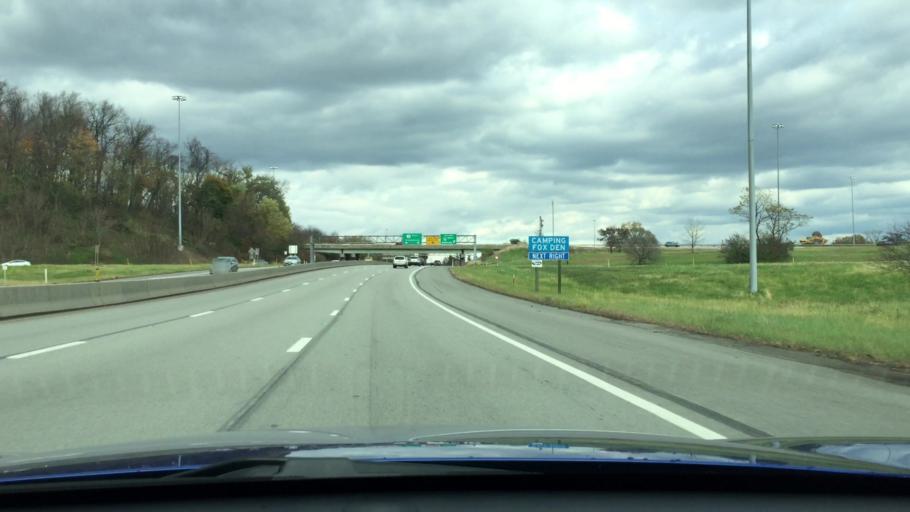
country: US
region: Pennsylvania
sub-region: Westmoreland County
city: New Stanton
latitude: 40.2239
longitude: -79.5963
